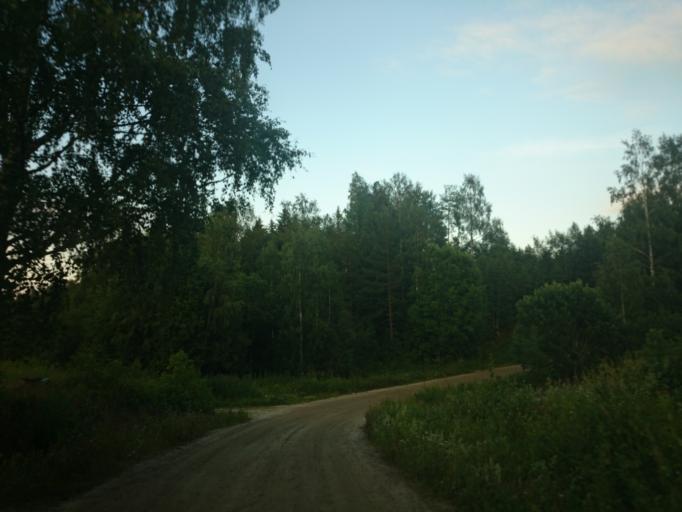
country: SE
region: Vaesternorrland
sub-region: Sundsvalls Kommun
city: Njurundabommen
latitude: 62.2023
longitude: 17.2701
